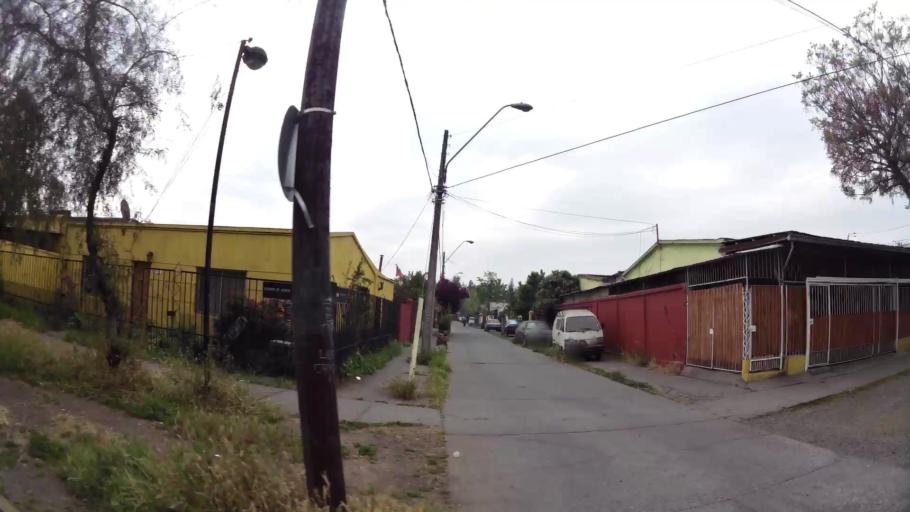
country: CL
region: Santiago Metropolitan
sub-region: Provincia de Santiago
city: Santiago
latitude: -33.4746
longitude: -70.6169
